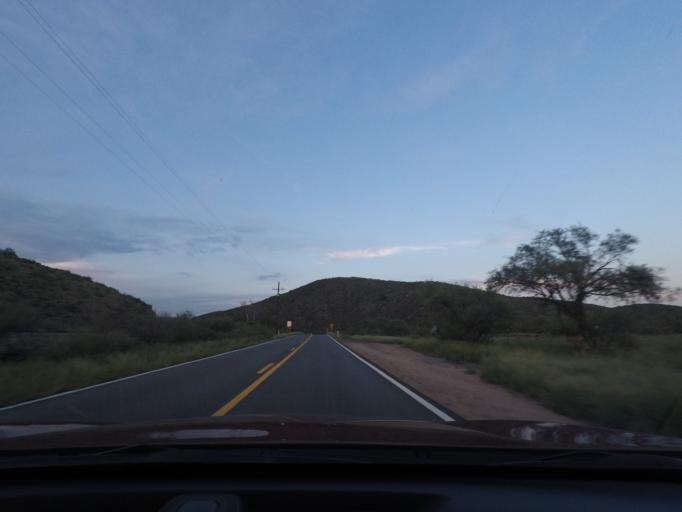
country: US
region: Arizona
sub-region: Yavapai County
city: Prescott
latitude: 34.4199
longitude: -112.7032
